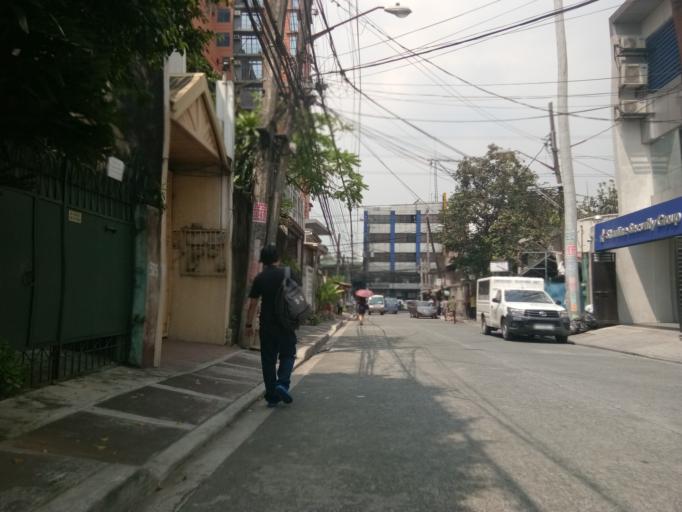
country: PH
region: Metro Manila
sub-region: Quezon City
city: Quezon City
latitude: 14.6191
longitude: 121.0590
